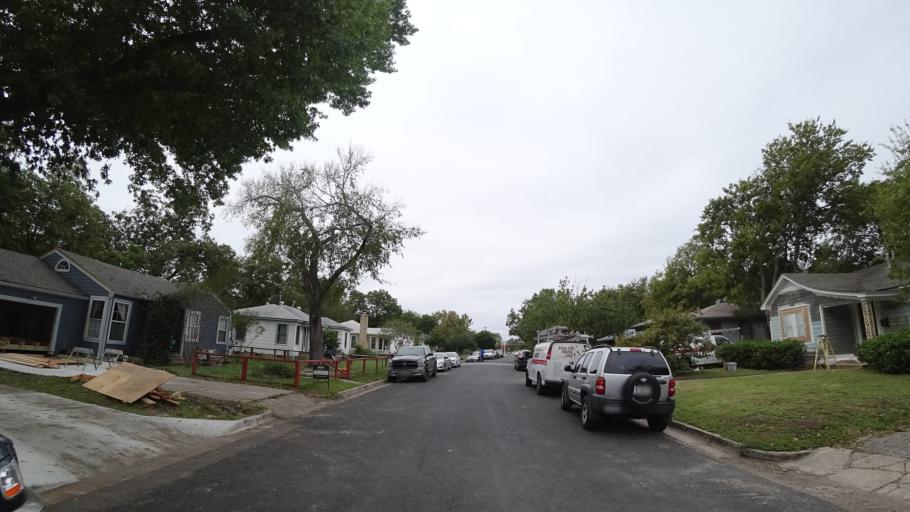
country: US
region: Texas
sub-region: Travis County
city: Austin
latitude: 30.2854
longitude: -97.7190
